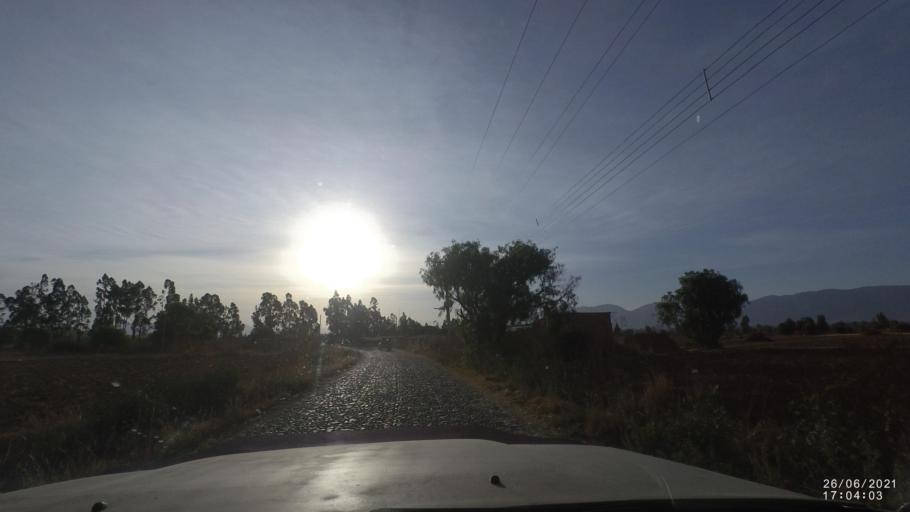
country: BO
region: Cochabamba
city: Cliza
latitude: -17.6379
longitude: -65.9141
